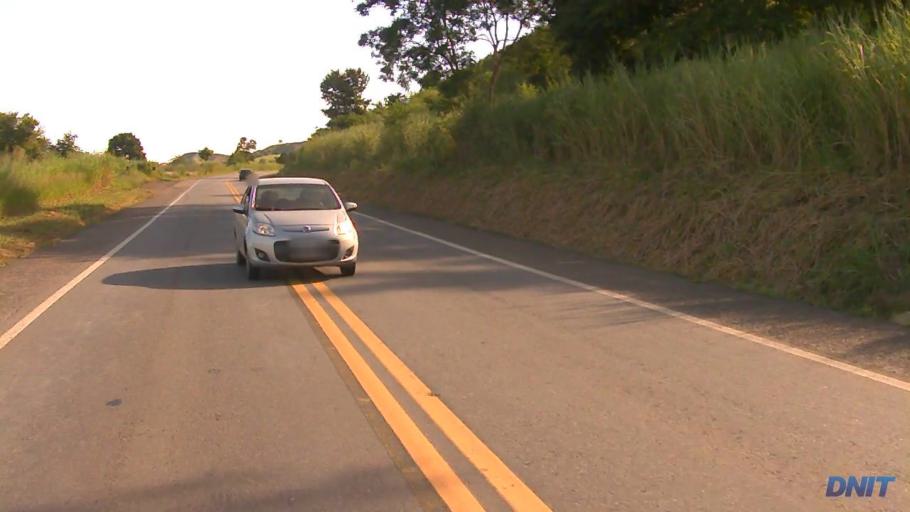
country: BR
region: Minas Gerais
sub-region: Belo Oriente
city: Belo Oriente
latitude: -19.1844
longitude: -42.2640
